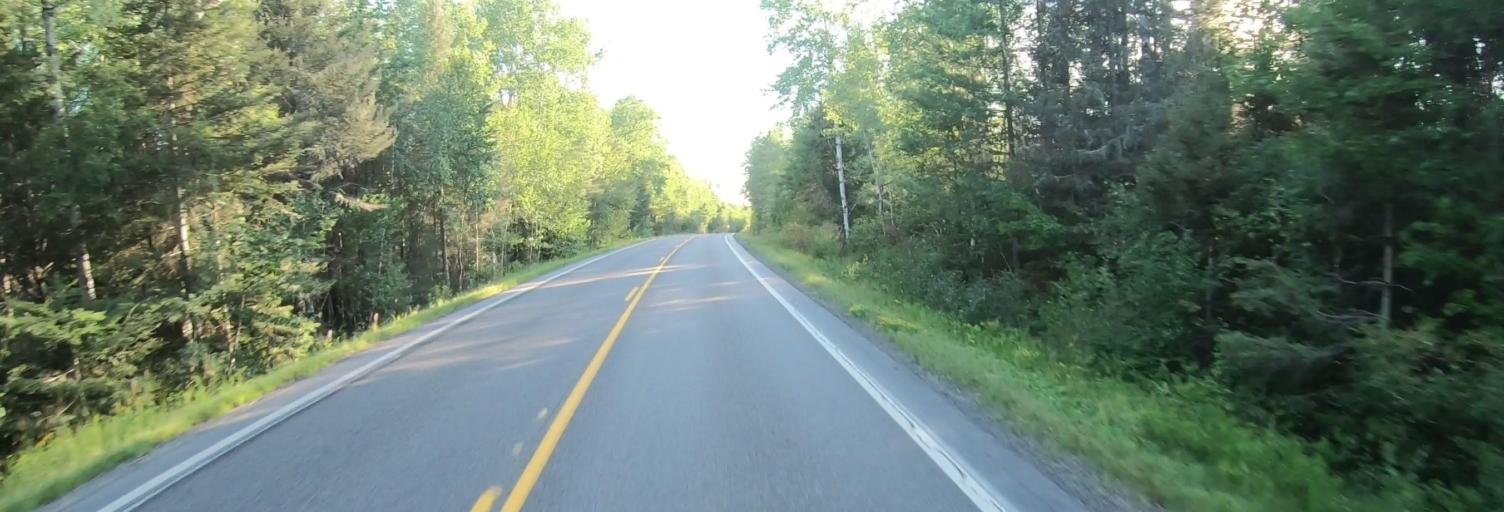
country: US
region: Minnesota
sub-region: Saint Louis County
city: Ely
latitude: 47.9367
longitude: -91.6830
